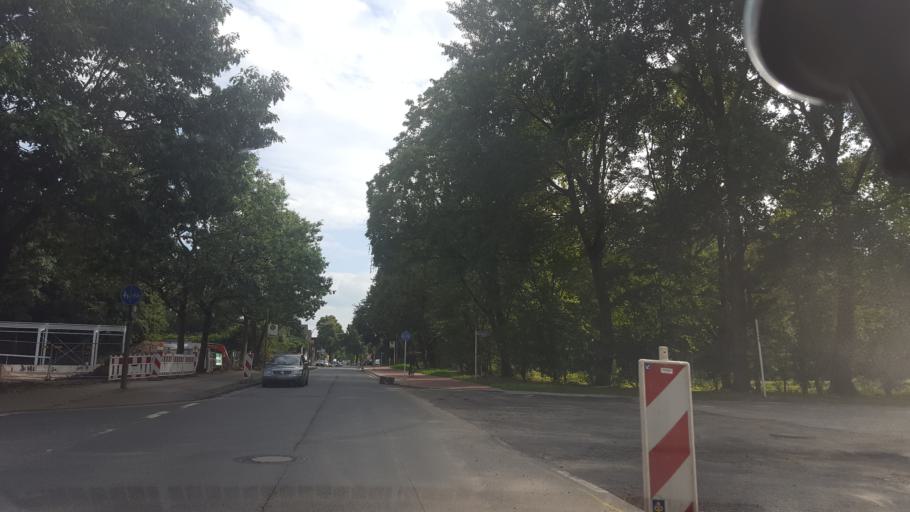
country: DE
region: North Rhine-Westphalia
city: Marl
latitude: 51.6662
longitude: 7.0917
